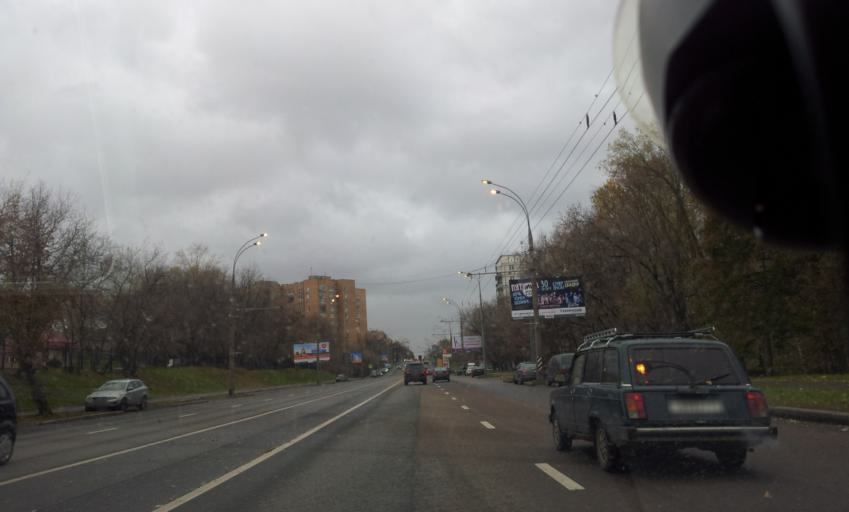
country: RU
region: Moscow
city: Vorob'yovo
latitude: 55.7211
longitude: 37.5252
